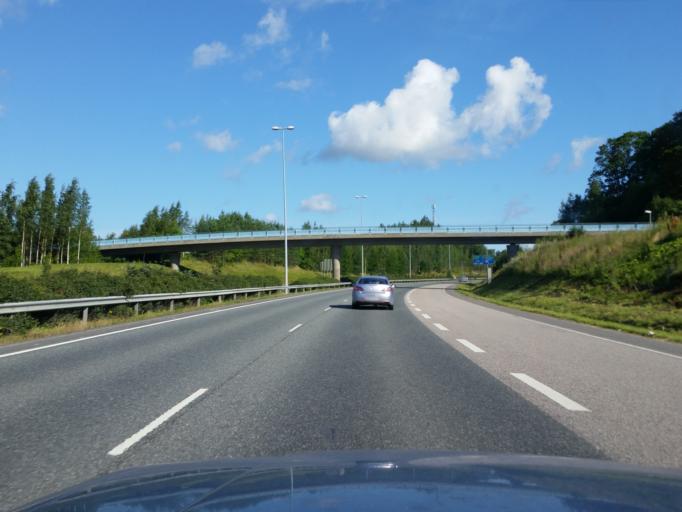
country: FI
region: Uusimaa
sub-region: Helsinki
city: Kauniainen
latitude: 60.1926
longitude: 24.7446
